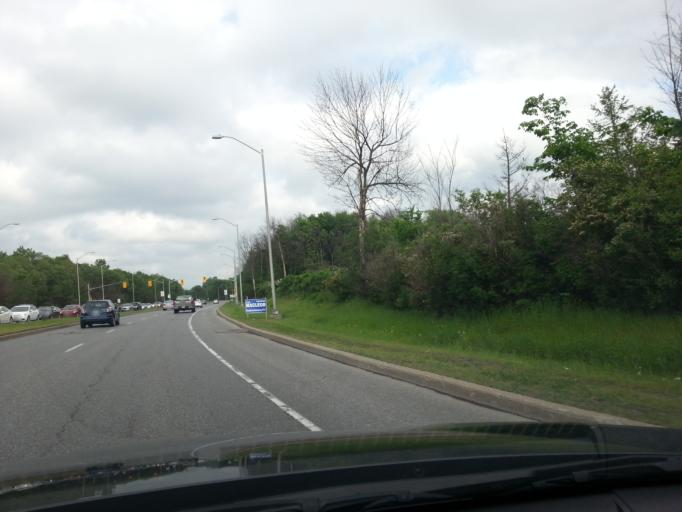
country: CA
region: Ontario
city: Bells Corners
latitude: 45.3298
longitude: -75.7465
